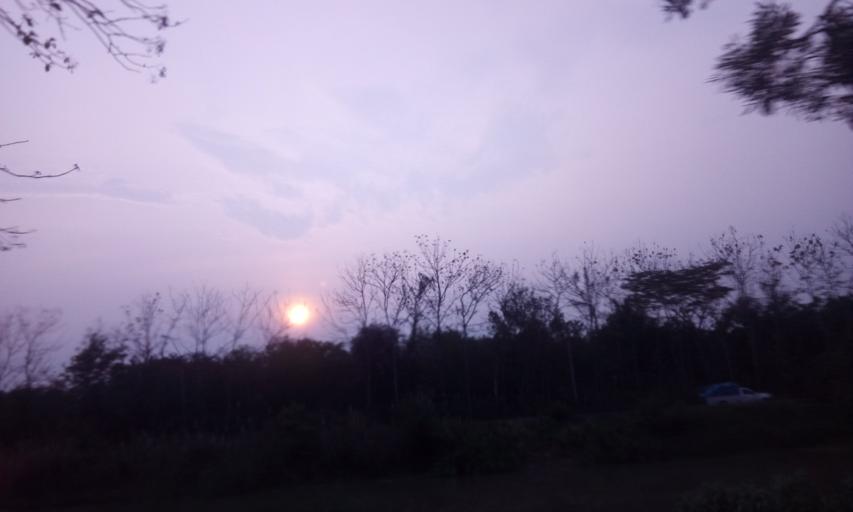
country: TH
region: Bangkok
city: Nong Chok
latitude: 13.9090
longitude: 100.8898
